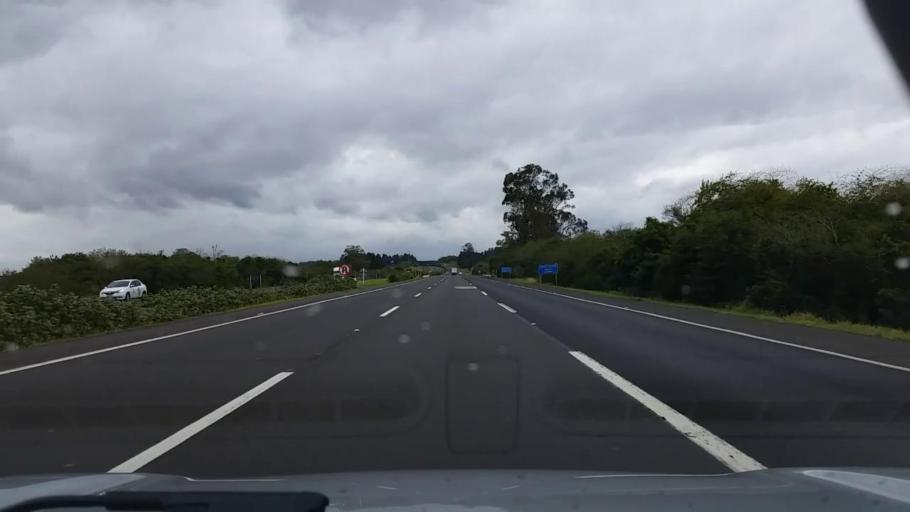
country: BR
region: Rio Grande do Sul
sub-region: Gravatai
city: Gravatai
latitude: -29.9215
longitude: -50.8426
